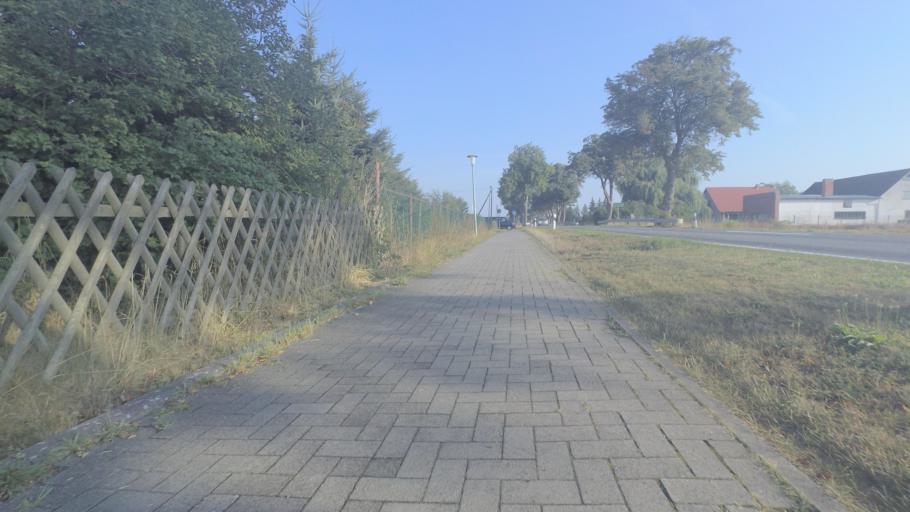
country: DE
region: Mecklenburg-Vorpommern
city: Gormin
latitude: 53.9894
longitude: 13.1500
